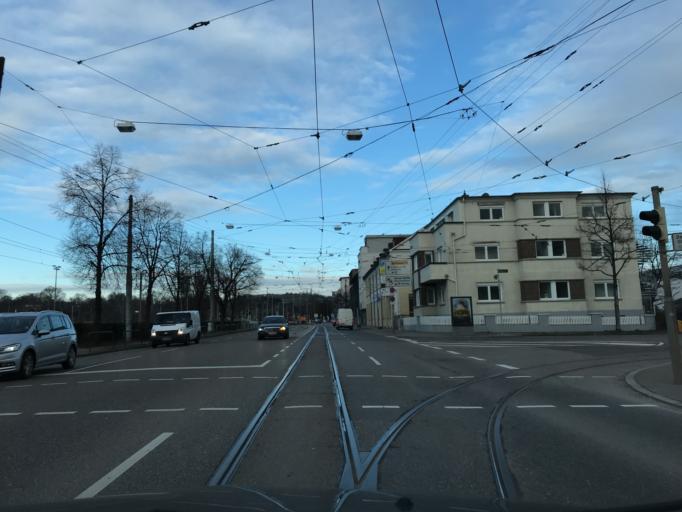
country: DE
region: Baden-Wuerttemberg
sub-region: Regierungsbezirk Stuttgart
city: Stuttgart-Ost
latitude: 48.7984
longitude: 9.2175
